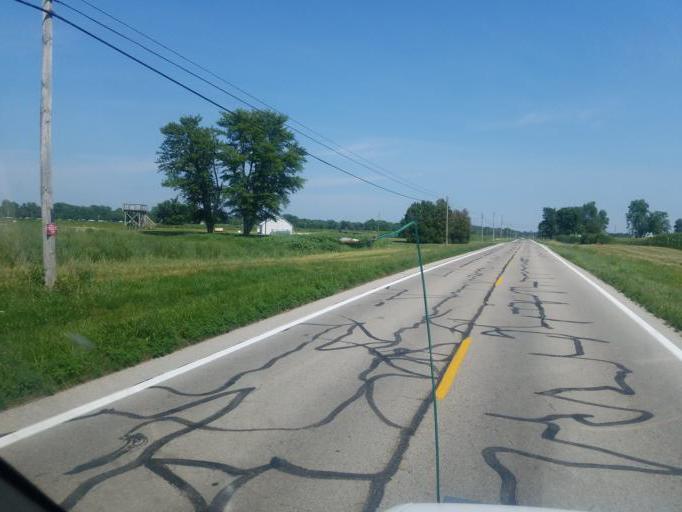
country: US
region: Ohio
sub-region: Mercer County
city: Celina
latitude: 40.4978
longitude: -84.5687
